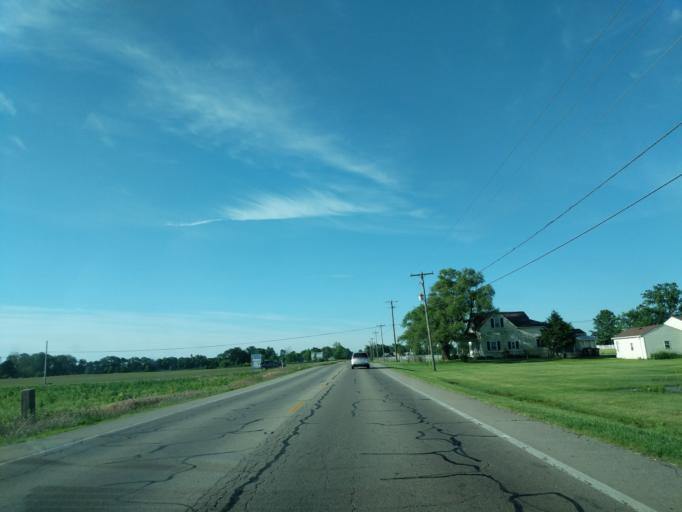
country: US
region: Indiana
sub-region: Madison County
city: Ingalls
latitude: 39.8875
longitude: -85.7705
